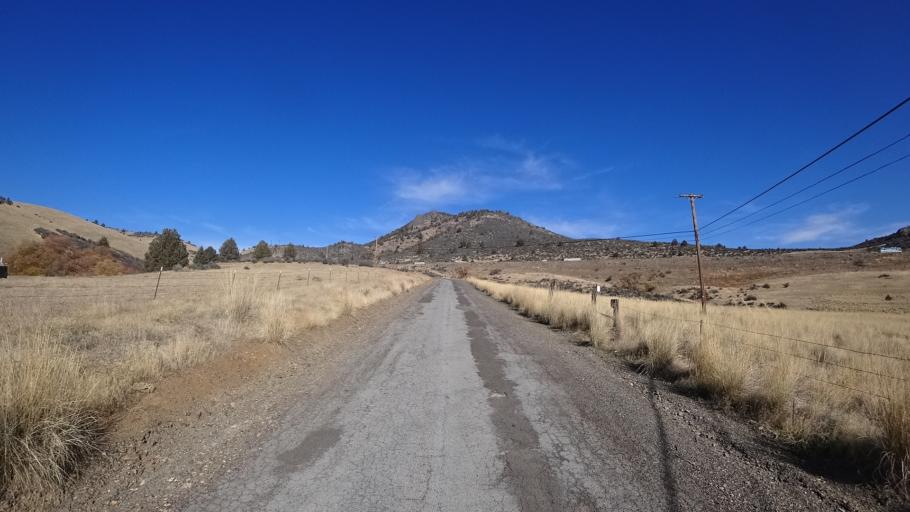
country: US
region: California
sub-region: Siskiyou County
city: Yreka
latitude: 41.7794
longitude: -122.5869
